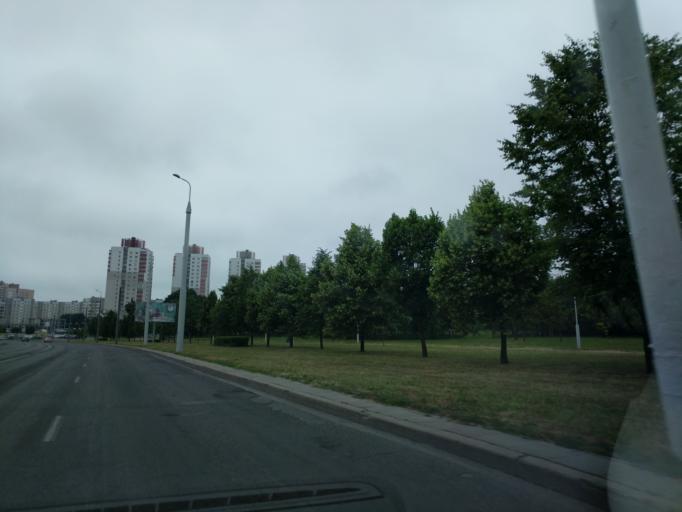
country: BY
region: Minsk
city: Malinovka
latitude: 53.8563
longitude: 27.4519
